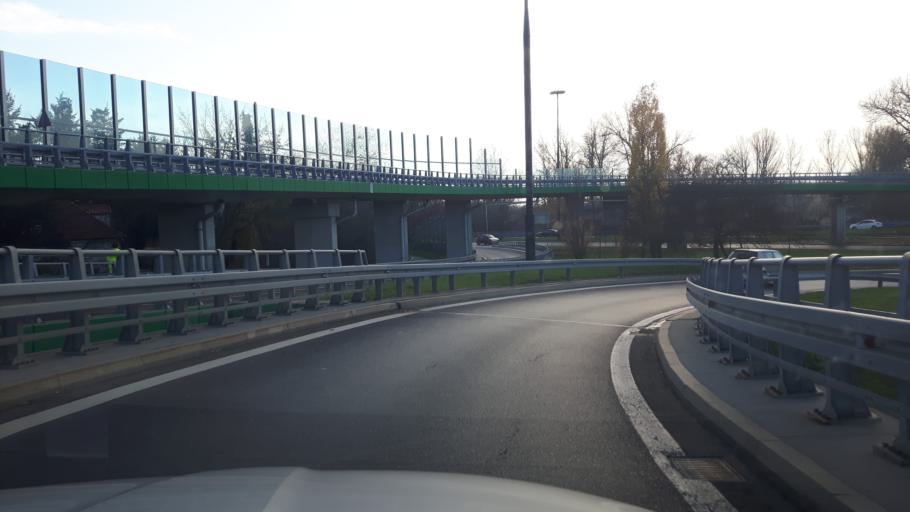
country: PL
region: Masovian Voivodeship
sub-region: Warszawa
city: Praga Poludnie
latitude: 52.2262
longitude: 21.0563
